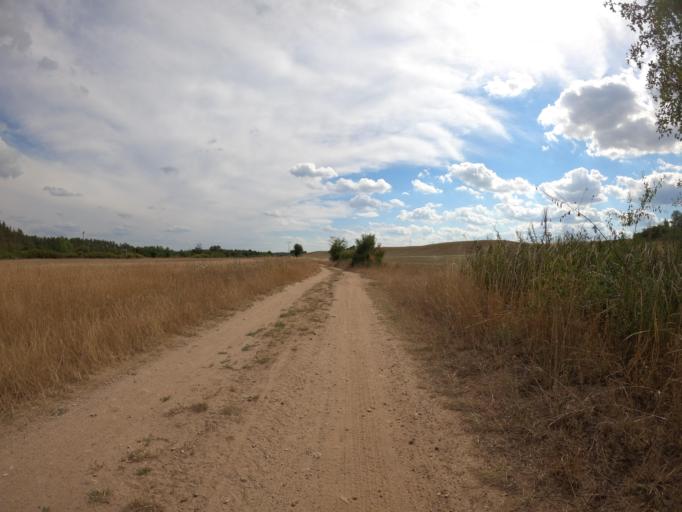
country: DE
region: Mecklenburg-Vorpommern
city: Loitz
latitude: 53.3250
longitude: 13.4288
